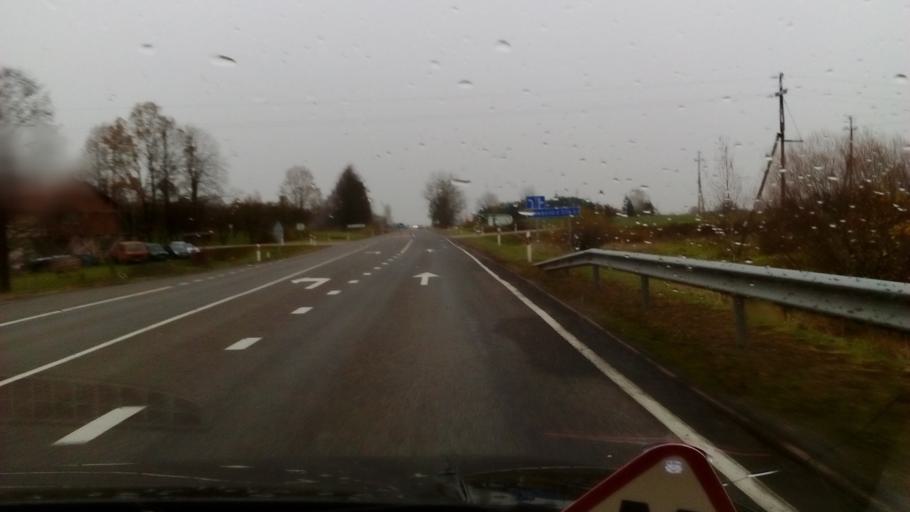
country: LT
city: Prienai
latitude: 54.5700
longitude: 23.7631
